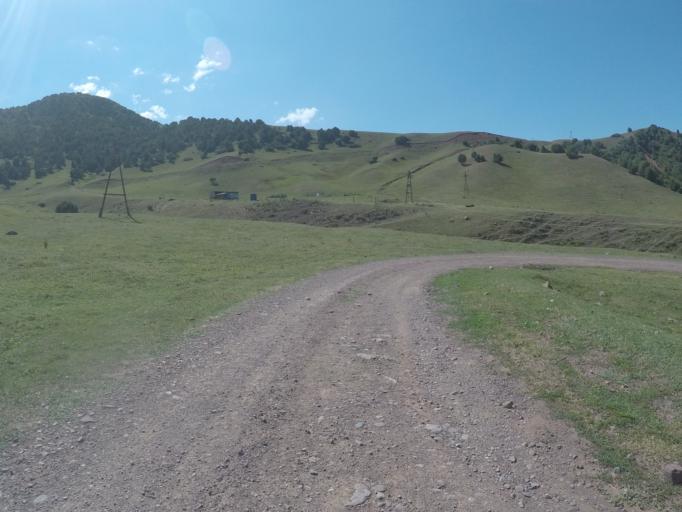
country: KG
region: Chuy
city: Bishkek
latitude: 42.6459
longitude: 74.5732
